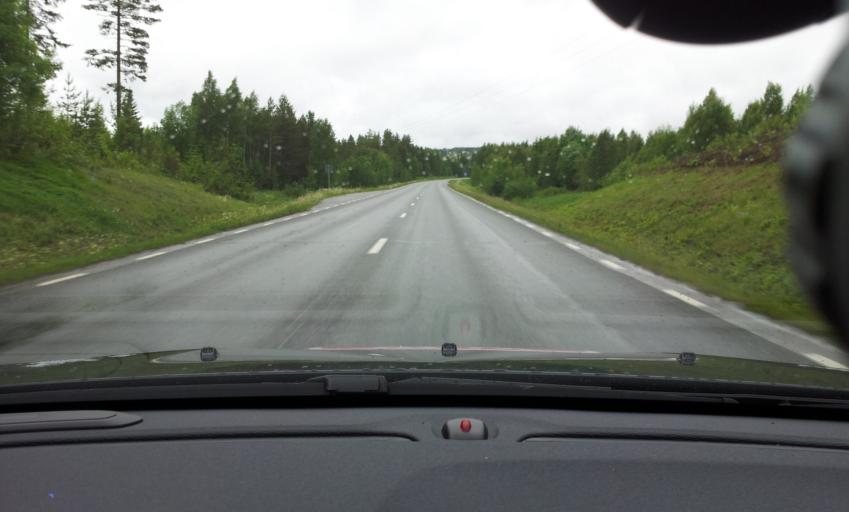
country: SE
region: Jaemtland
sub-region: Krokoms Kommun
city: Krokom
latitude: 63.3465
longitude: 14.4748
